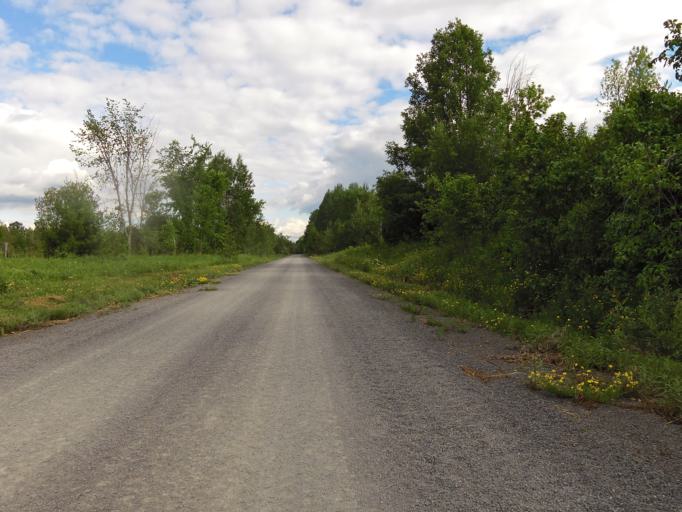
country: CA
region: Ontario
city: Arnprior
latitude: 45.2991
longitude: -76.2639
